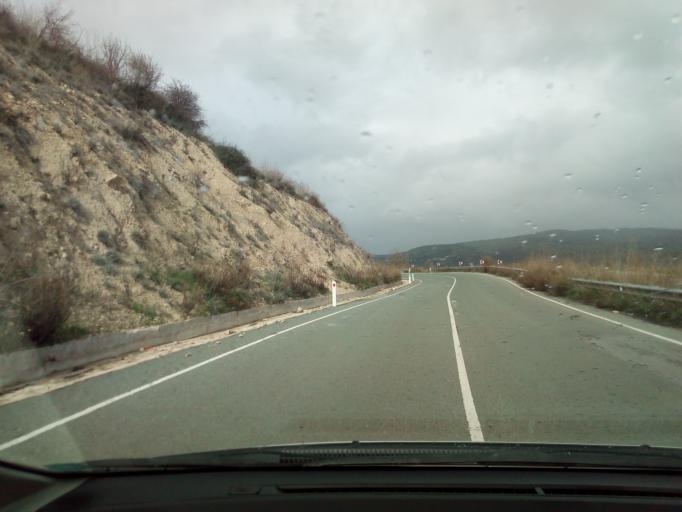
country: CY
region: Pafos
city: Tala
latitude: 34.9374
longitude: 32.5159
